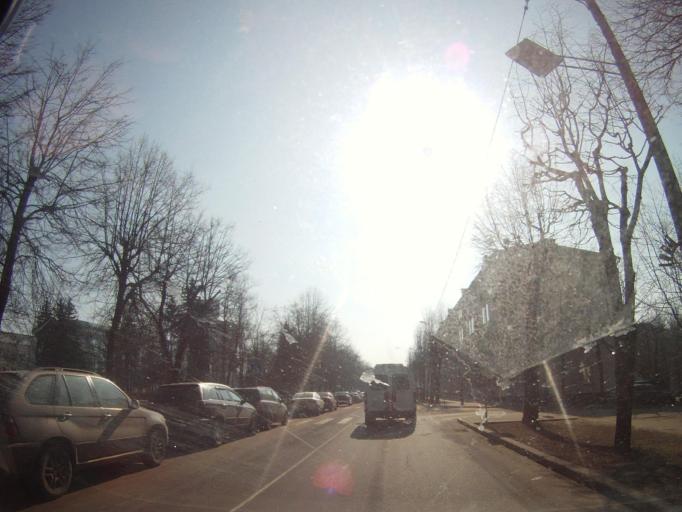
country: BY
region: Minsk
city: Minsk
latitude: 53.9269
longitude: 27.6121
